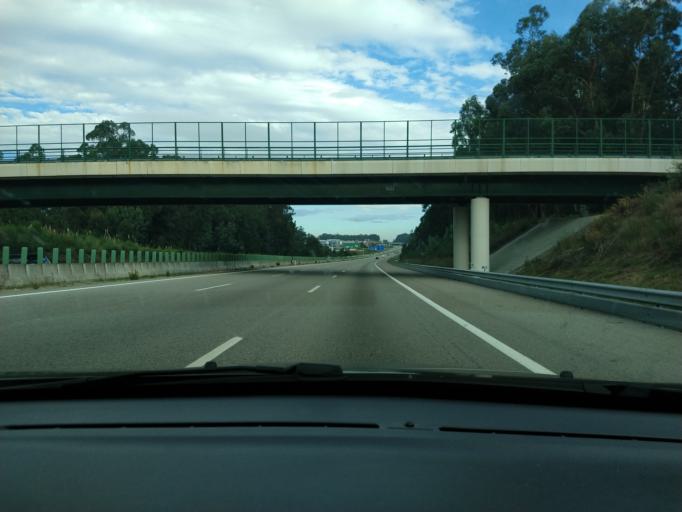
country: PT
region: Aveiro
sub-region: Santa Maria da Feira
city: Feira
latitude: 40.9110
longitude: -8.5675
